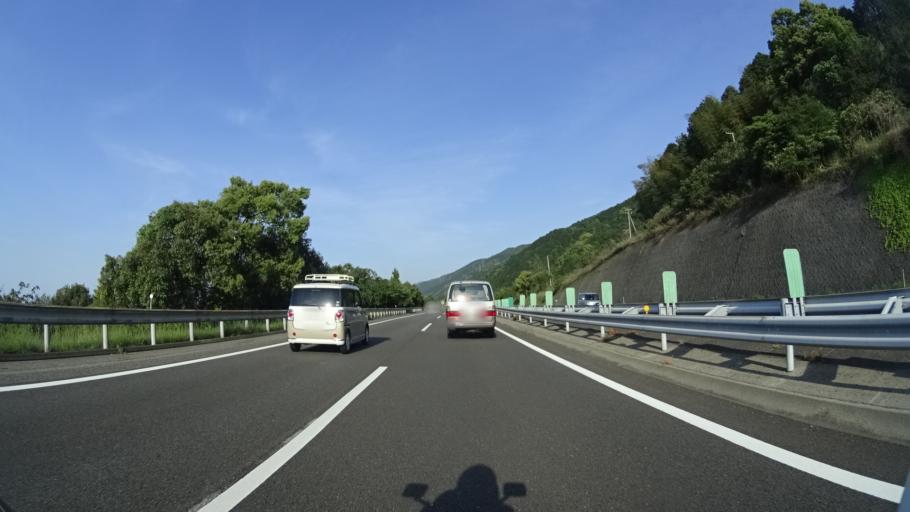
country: JP
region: Ehime
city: Kawanoecho
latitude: 33.9602
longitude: 133.5002
